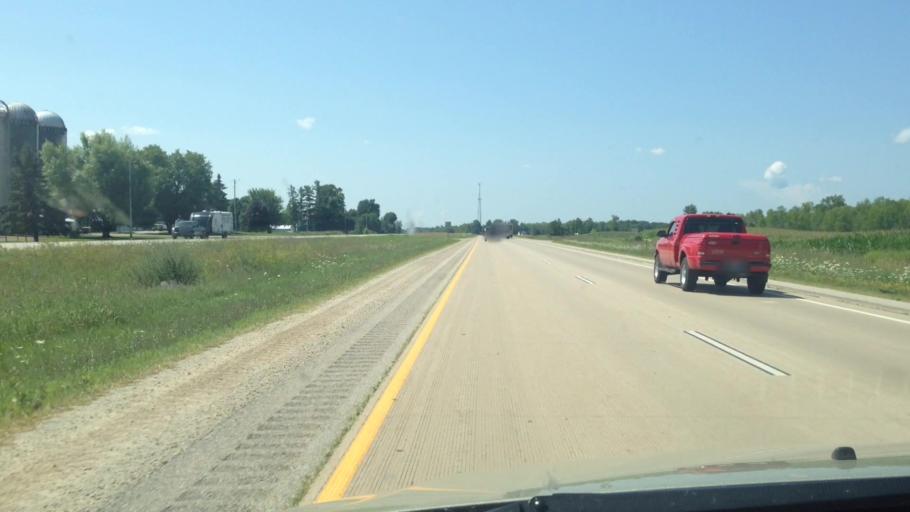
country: US
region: Wisconsin
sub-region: Marinette County
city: Peshtigo
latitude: 45.0105
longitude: -87.8444
